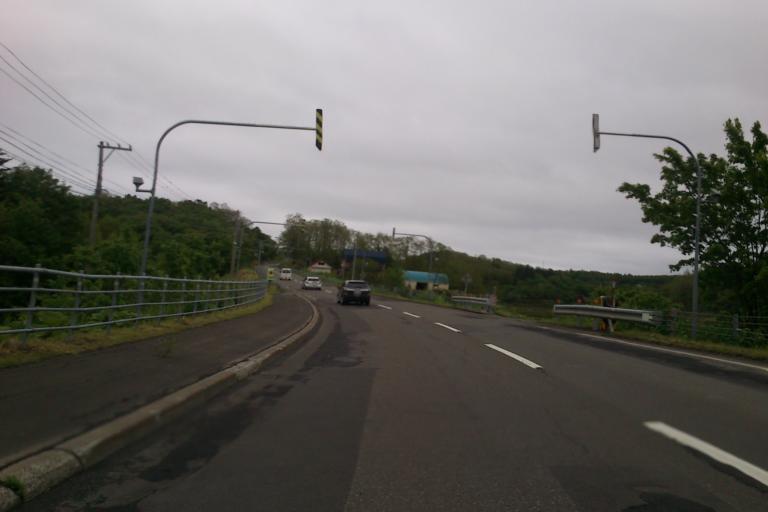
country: JP
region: Hokkaido
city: Ishikari
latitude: 43.3241
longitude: 141.4434
